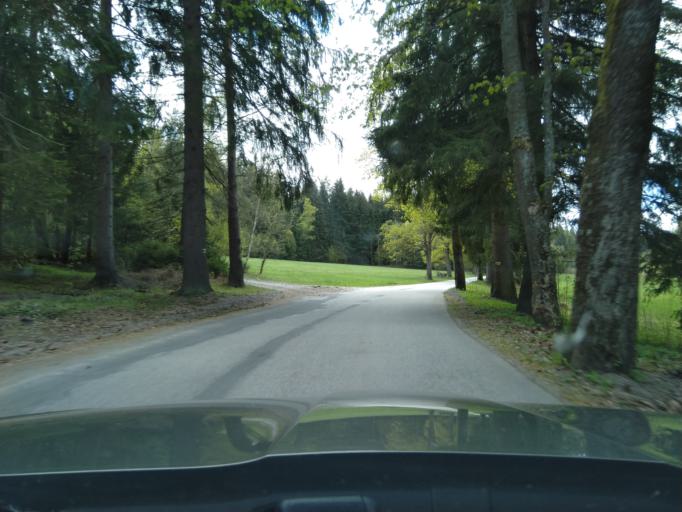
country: CZ
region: Jihocesky
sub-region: Okres Prachatice
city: Vimperk
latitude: 49.0253
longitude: 13.7526
